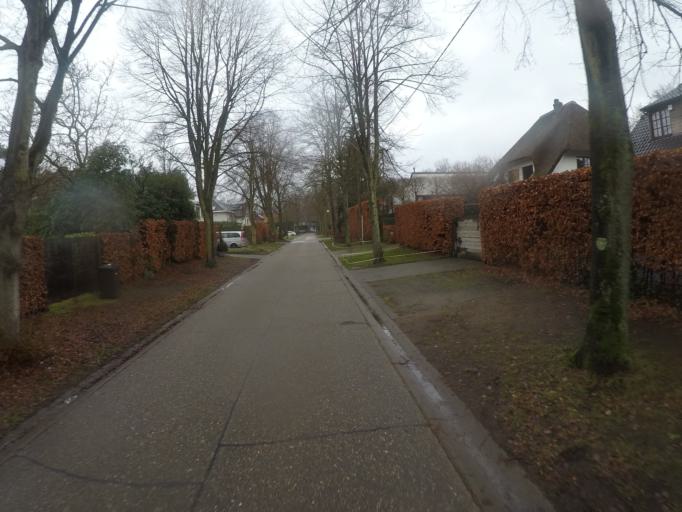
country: BE
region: Flanders
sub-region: Provincie Antwerpen
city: Schilde
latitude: 51.2308
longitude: 4.5555
